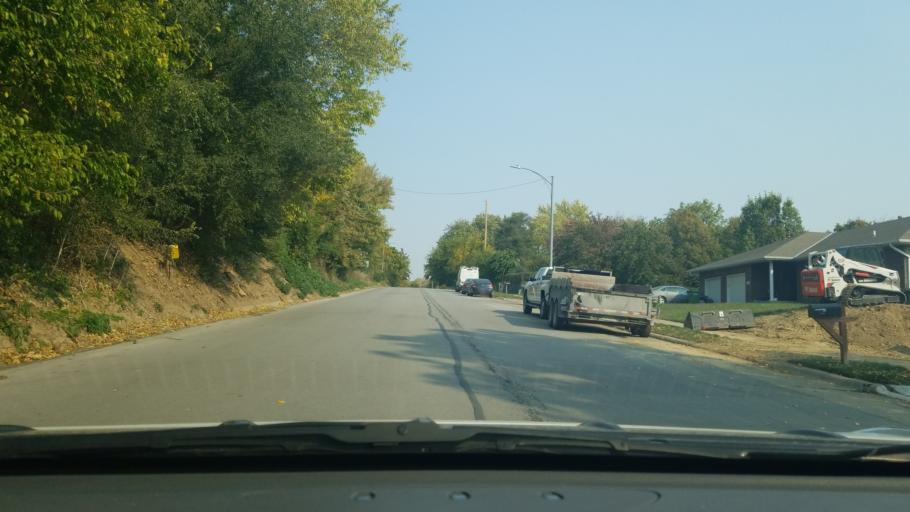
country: US
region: Nebraska
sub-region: Sarpy County
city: Bellevue
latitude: 41.1562
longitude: -95.9091
